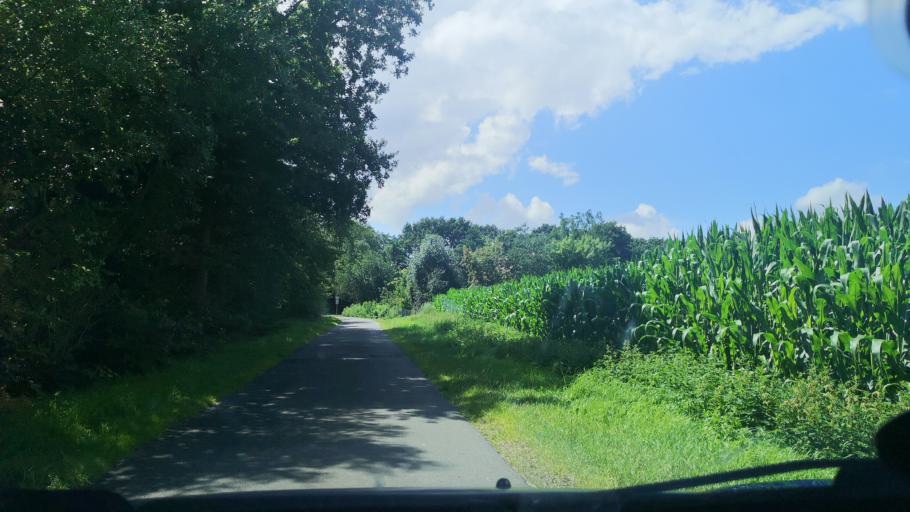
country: DE
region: Lower Saxony
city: Langen
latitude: 53.6405
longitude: 8.6137
